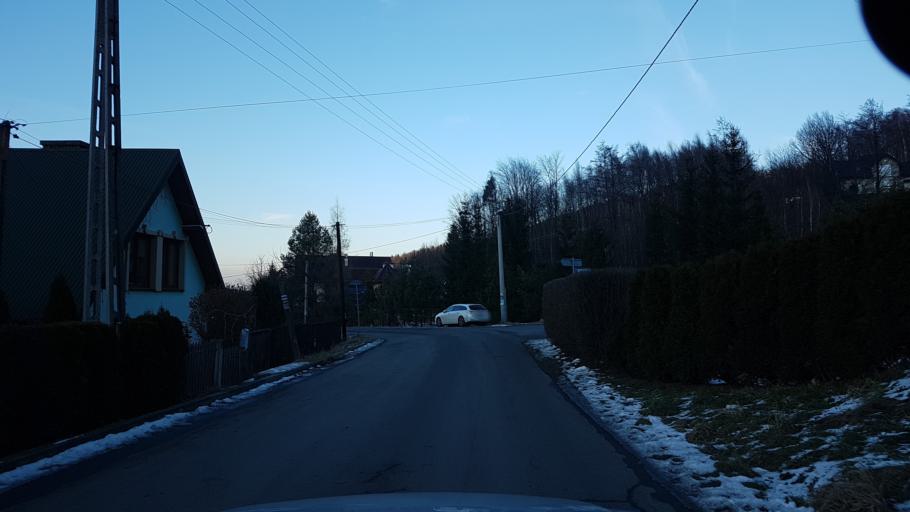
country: PL
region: Lesser Poland Voivodeship
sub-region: Powiat nowosadecki
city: Rytro
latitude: 49.5192
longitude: 20.6634
